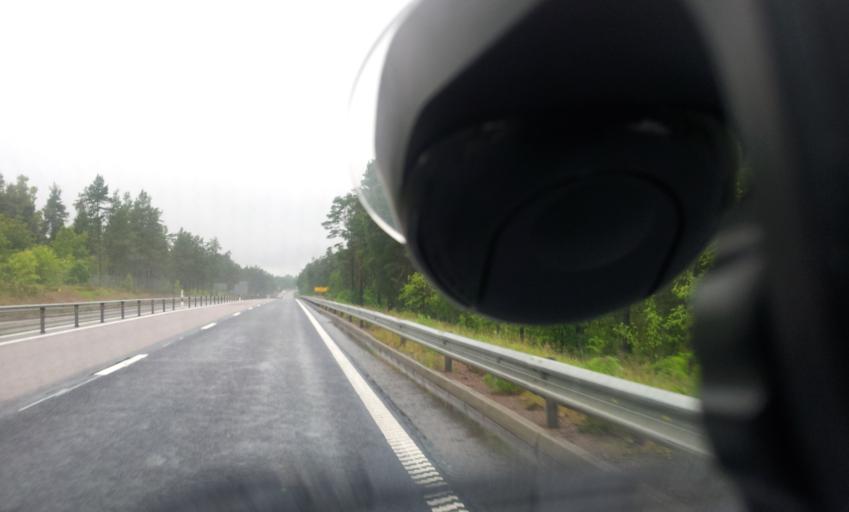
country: SE
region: Kalmar
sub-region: Oskarshamns Kommun
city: Oskarshamn
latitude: 57.3837
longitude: 16.4813
